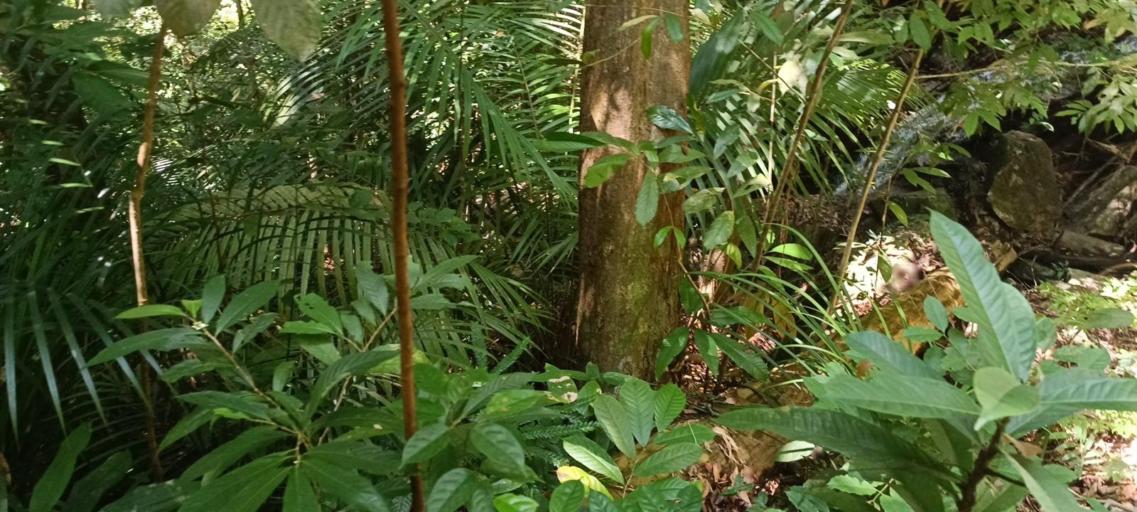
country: MY
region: Penang
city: Tanjung Tokong
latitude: 5.4335
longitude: 100.2896
